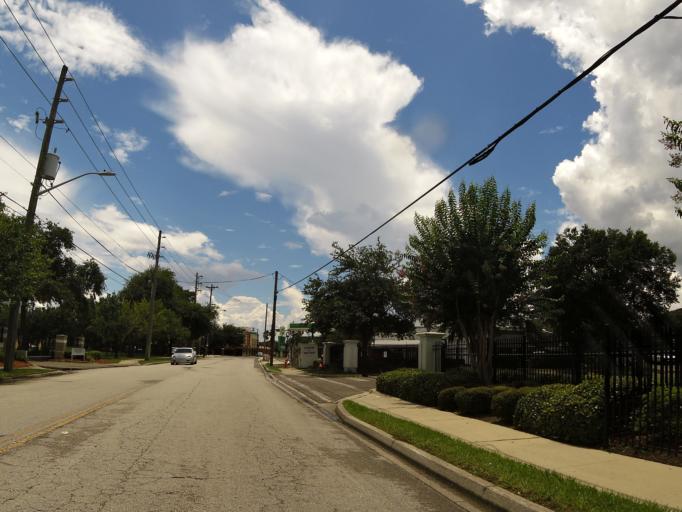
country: US
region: Florida
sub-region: Duval County
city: Jacksonville
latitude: 30.3369
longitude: -81.6670
